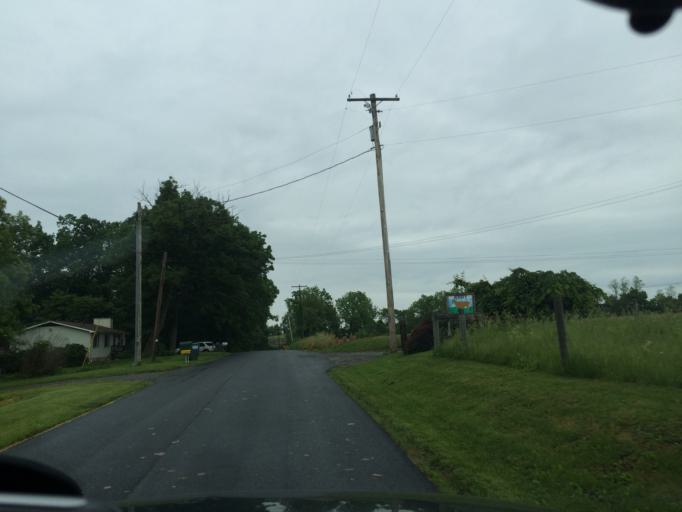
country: US
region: Maryland
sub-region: Carroll County
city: Taneytown
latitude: 39.5876
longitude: -77.2238
